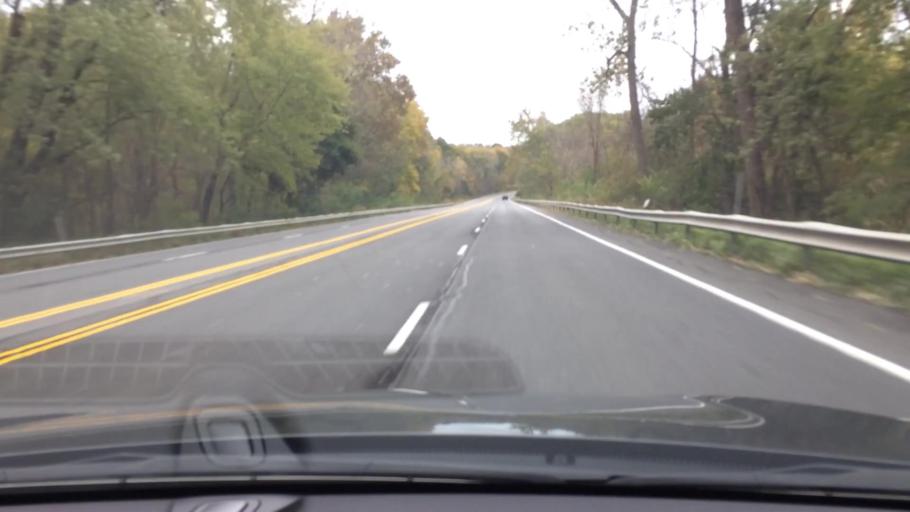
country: US
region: New York
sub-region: Columbia County
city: Kinderhook
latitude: 42.4022
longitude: -73.6884
